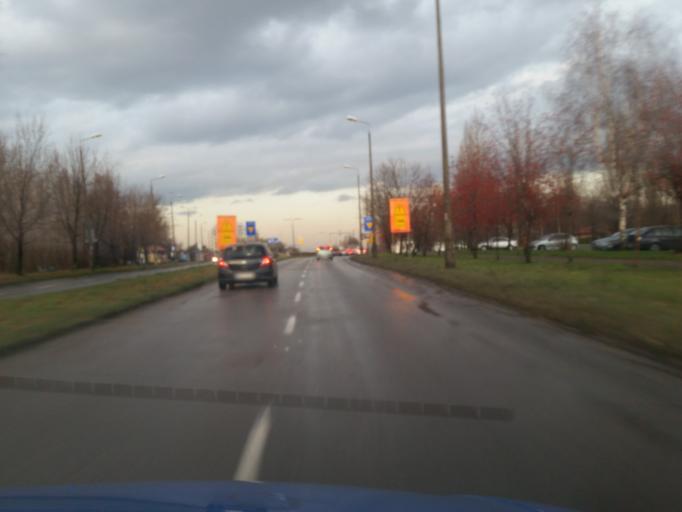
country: PL
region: Silesian Voivodeship
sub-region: Powiat bedzinski
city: Bedzin
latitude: 50.2833
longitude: 19.1770
